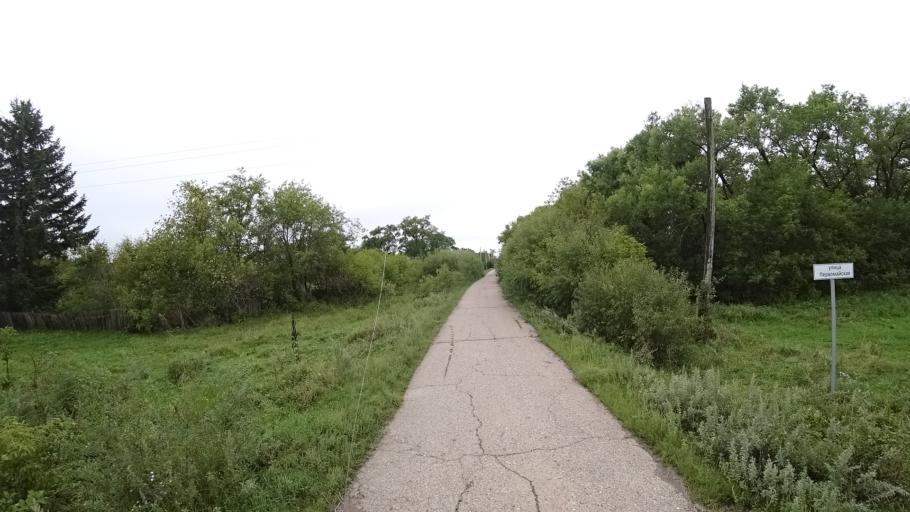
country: RU
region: Primorskiy
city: Monastyrishche
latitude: 44.0826
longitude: 132.5891
